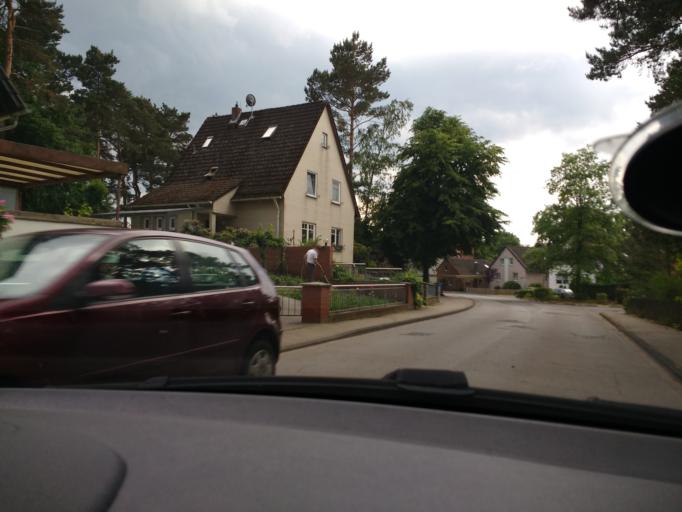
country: DE
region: Lower Saxony
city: Gifhorn
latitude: 52.4757
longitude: 10.5402
